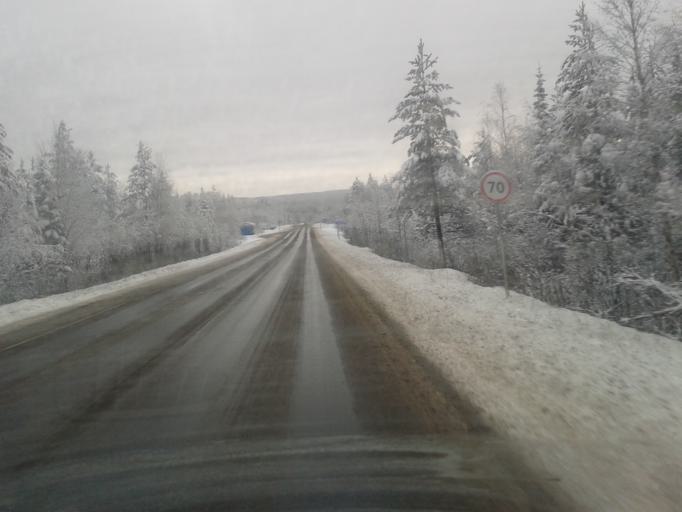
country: RU
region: Murmansk
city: Polyarnyye Zori
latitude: 67.3992
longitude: 32.5218
